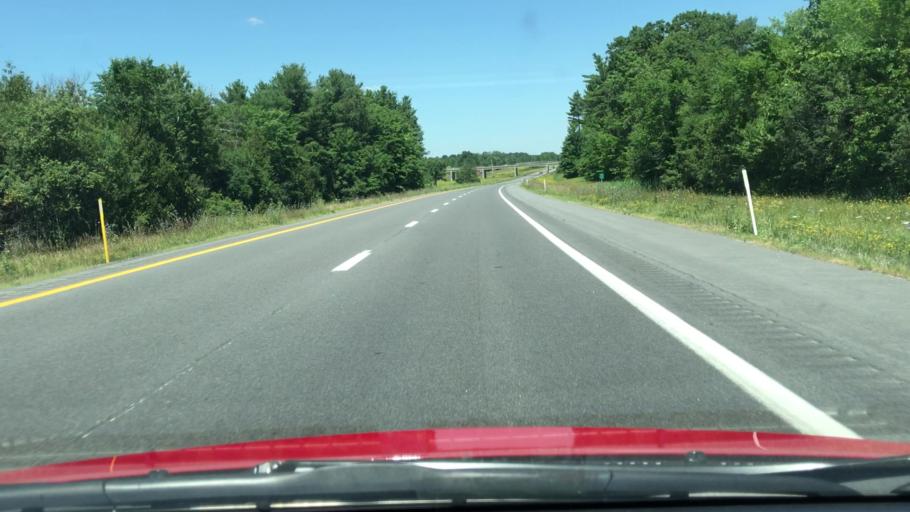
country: US
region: New York
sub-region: Clinton County
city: Cumberland Head
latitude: 44.8143
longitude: -73.4463
